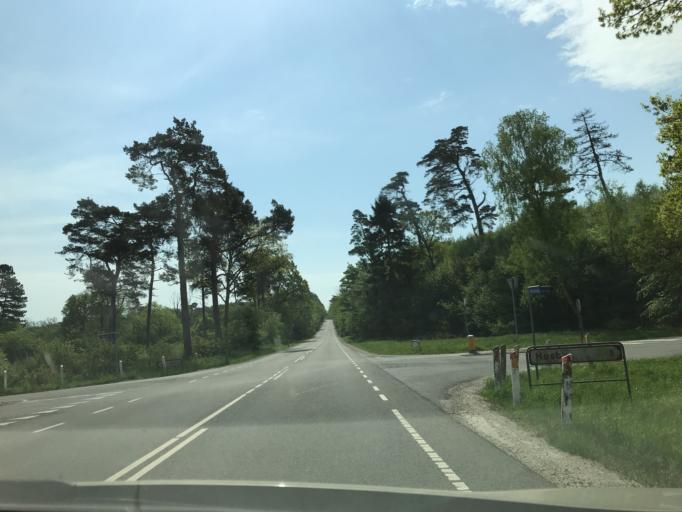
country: DK
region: South Denmark
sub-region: Middelfart Kommune
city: Ejby
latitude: 55.3982
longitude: 9.9039
